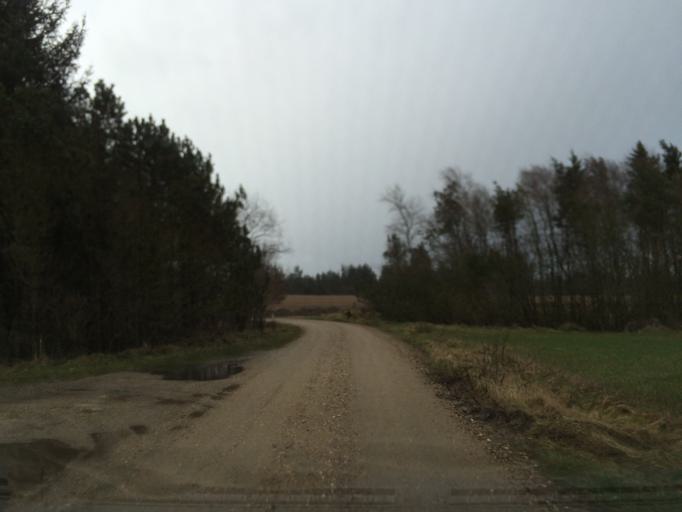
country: DK
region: Central Jutland
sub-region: Holstebro Kommune
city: Ulfborg
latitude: 56.2271
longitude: 8.4939
